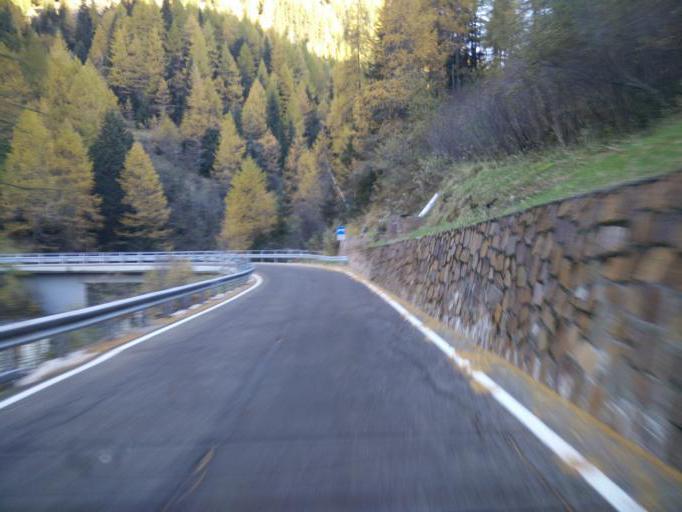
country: IT
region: Trentino-Alto Adige
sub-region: Bolzano
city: Moso in Passiria
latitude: 46.8799
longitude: 11.1641
